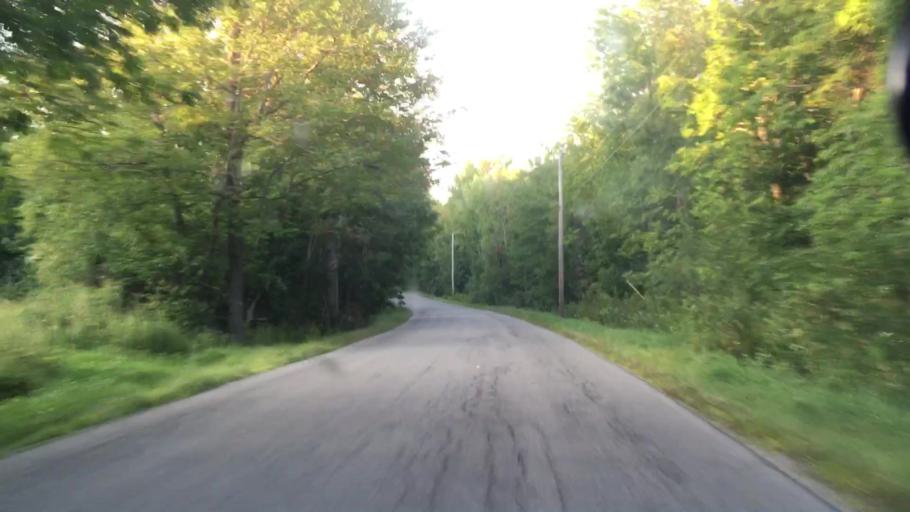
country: US
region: Maine
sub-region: Waldo County
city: Frankfort
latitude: 44.6691
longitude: -68.9259
